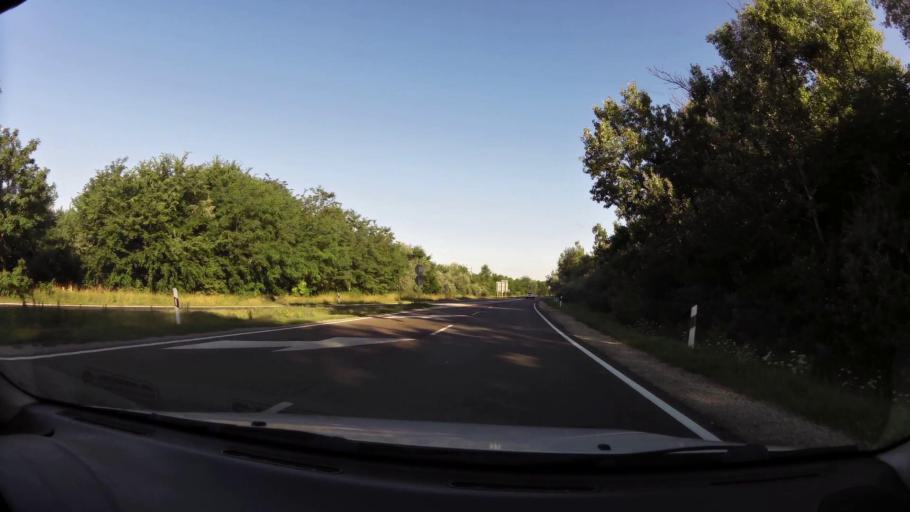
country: HU
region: Pest
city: Albertirsa
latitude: 47.2628
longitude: 19.5825
